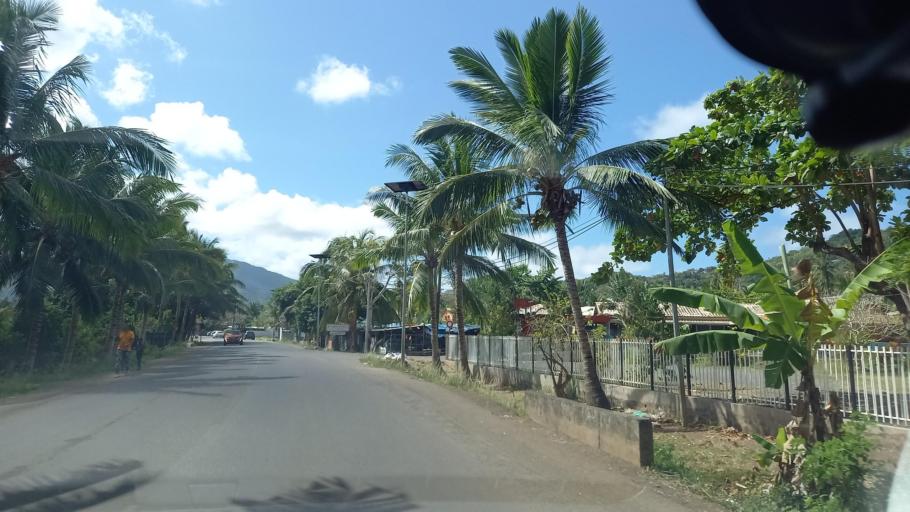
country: YT
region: Chirongui
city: Chirongui
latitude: -12.9321
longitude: 45.1523
